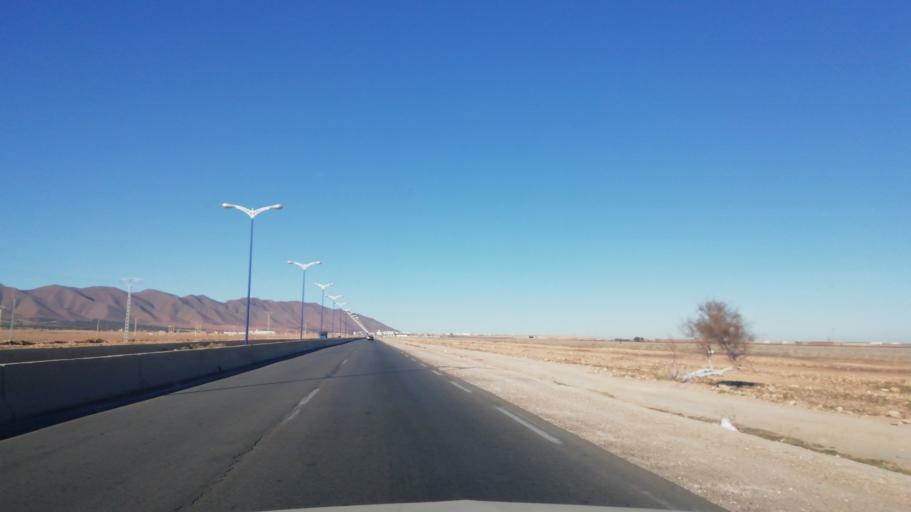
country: DZ
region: Wilaya de Naama
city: Naama
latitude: 33.4943
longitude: -0.2889
